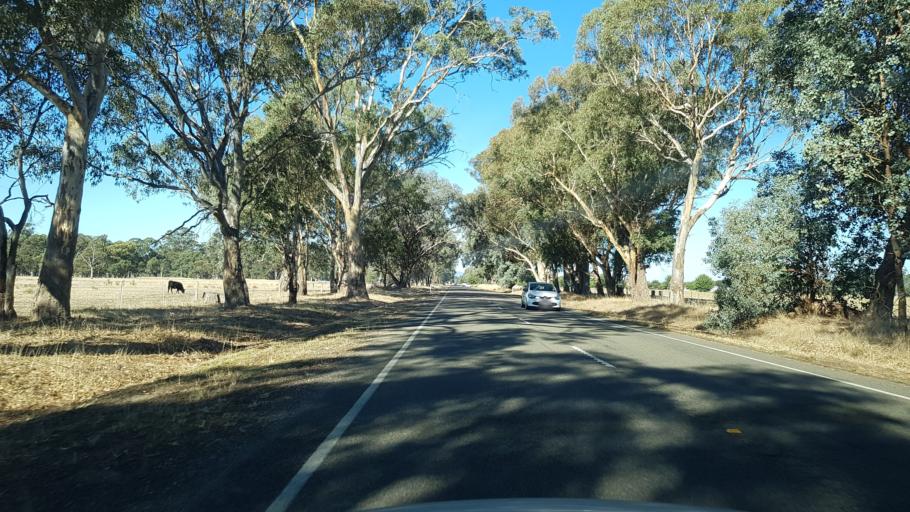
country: AU
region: Victoria
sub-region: Wangaratta
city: Wangaratta
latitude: -36.4375
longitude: 146.3388
